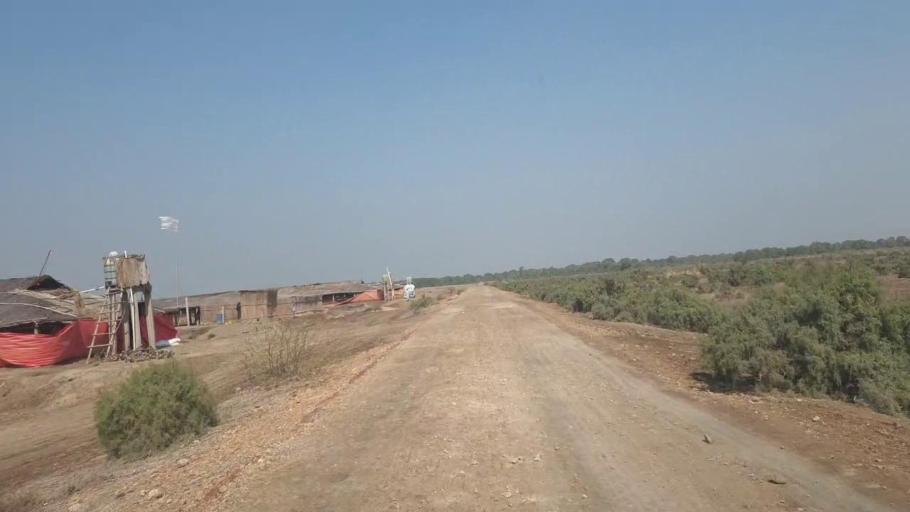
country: PK
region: Sindh
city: Tando Allahyar
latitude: 25.4406
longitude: 68.8359
